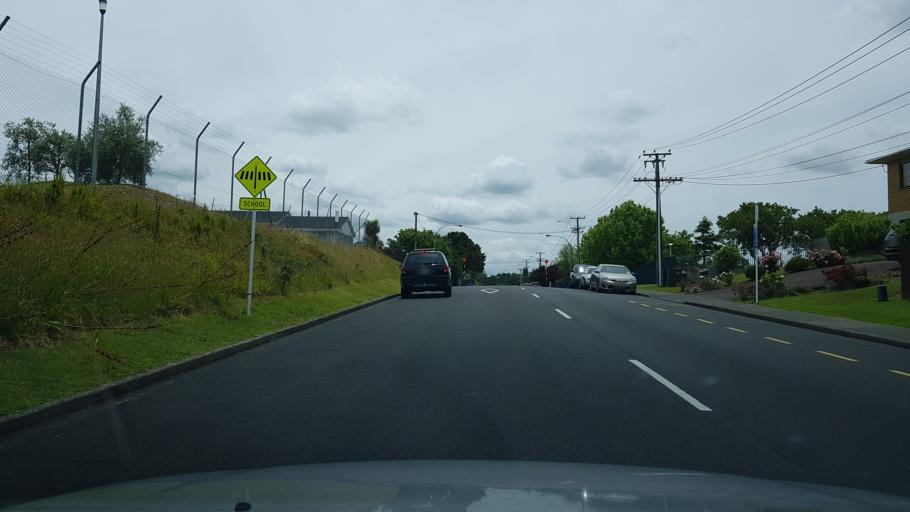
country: NZ
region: Auckland
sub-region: Auckland
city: North Shore
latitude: -36.8174
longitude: 174.7079
